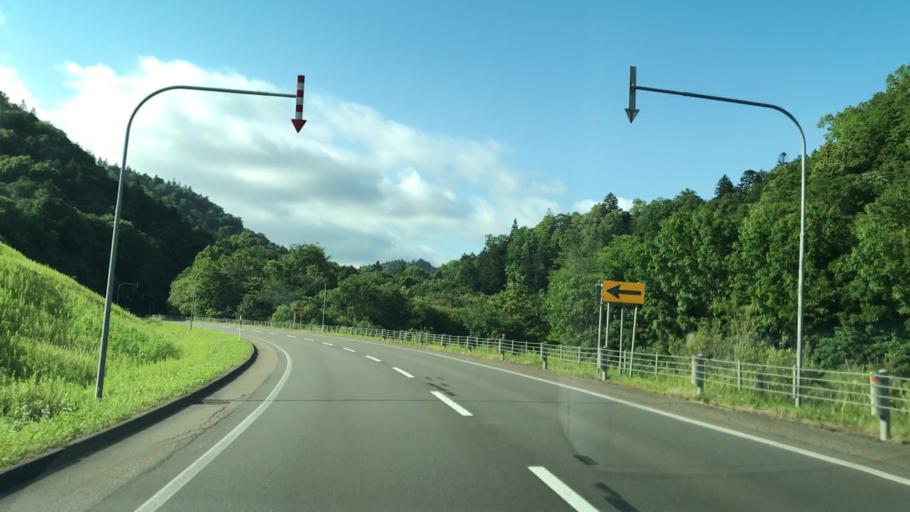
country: JP
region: Hokkaido
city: Chitose
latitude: 42.8842
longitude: 142.1237
